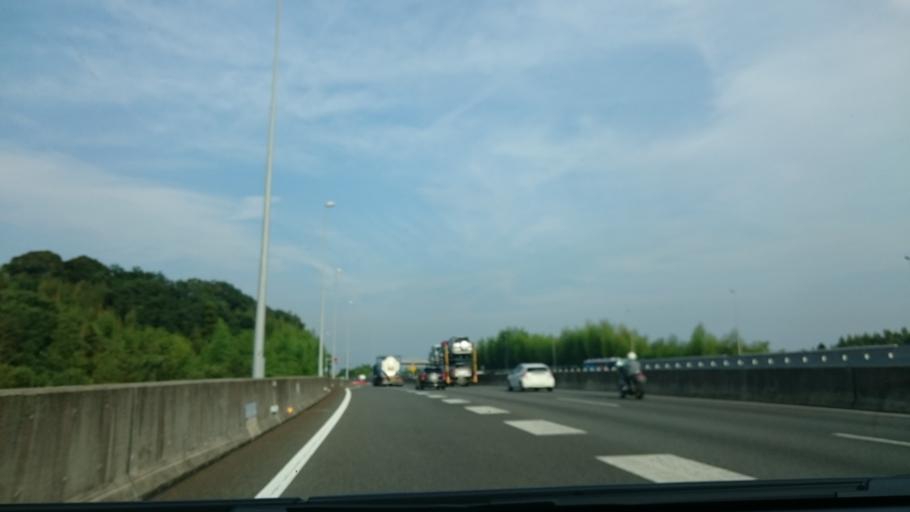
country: JP
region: Mie
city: Yokkaichi
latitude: 35.0372
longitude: 136.6322
